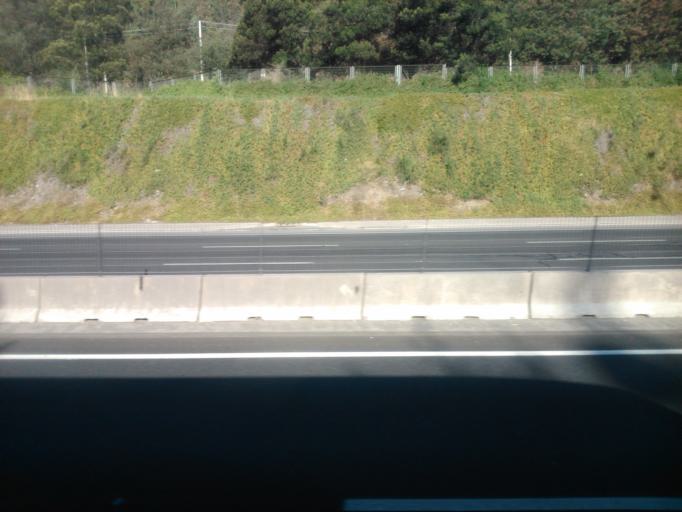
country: CL
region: Santiago Metropolitan
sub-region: Provincia de Maipo
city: San Bernardo
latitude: -33.6093
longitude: -70.7167
